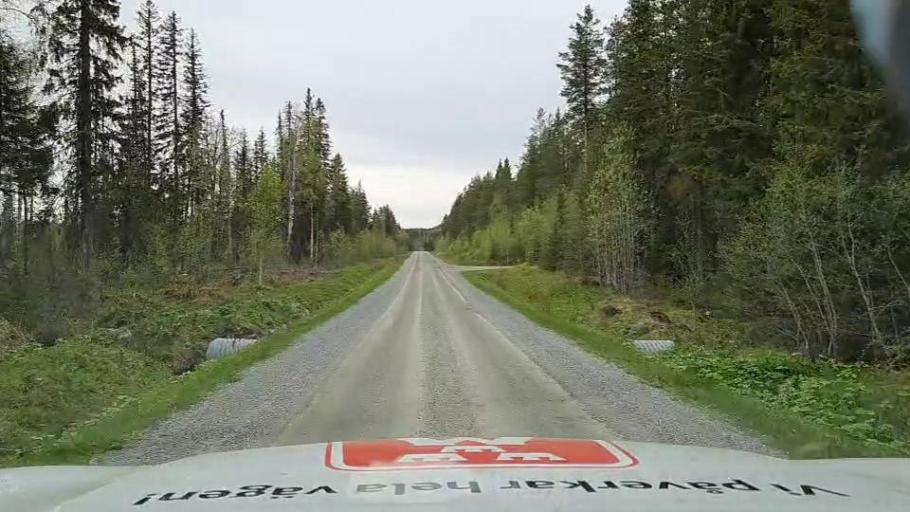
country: SE
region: Jaemtland
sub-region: OEstersunds Kommun
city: Brunflo
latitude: 62.6410
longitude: 14.9334
